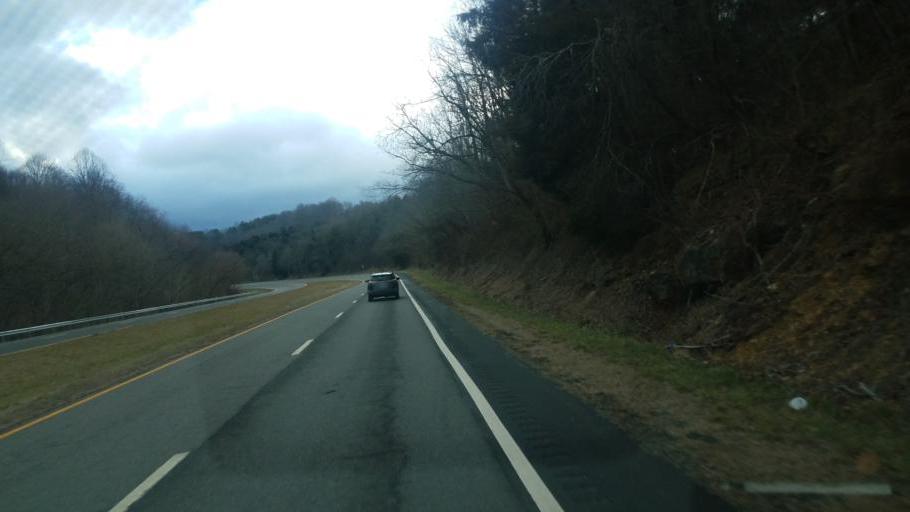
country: US
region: Virginia
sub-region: Giles County
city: Pearisburg
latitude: 37.2687
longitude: -80.7148
